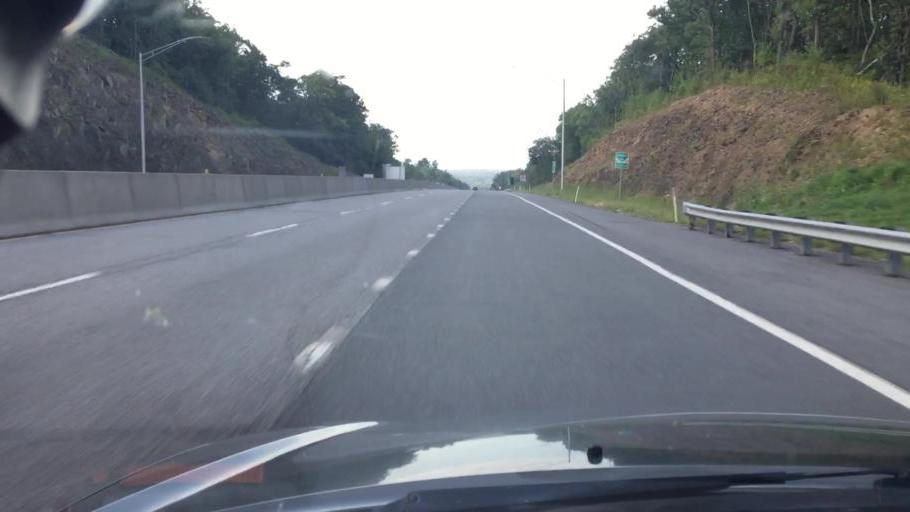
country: US
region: Pennsylvania
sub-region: Carbon County
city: Towamensing Trails
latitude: 40.9874
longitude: -75.6305
